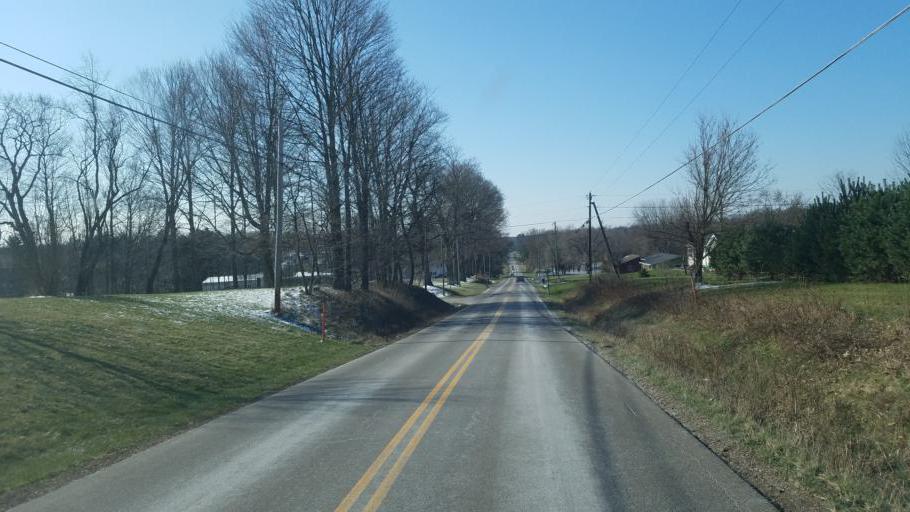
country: US
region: Ohio
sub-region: Knox County
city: Mount Vernon
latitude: 40.4276
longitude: -82.4877
